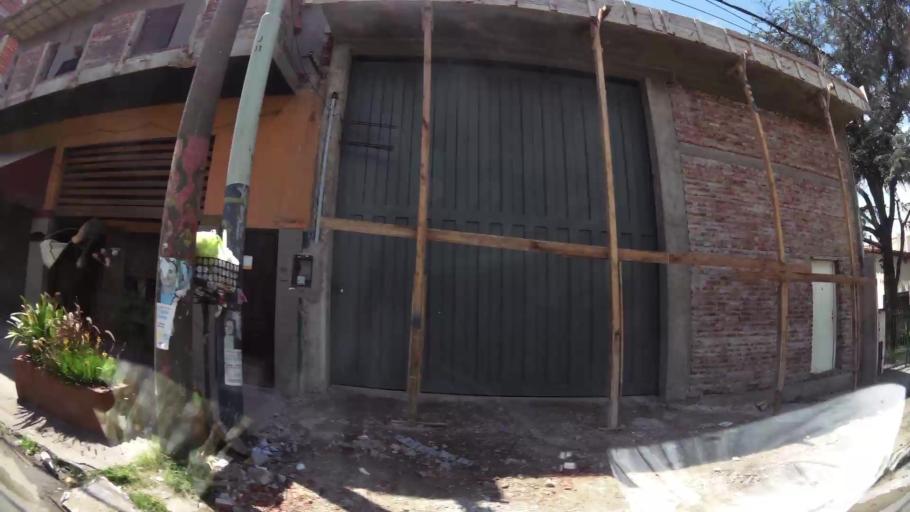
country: AR
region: Buenos Aires
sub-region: Partido de Quilmes
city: Quilmes
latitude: -34.7816
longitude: -58.2629
